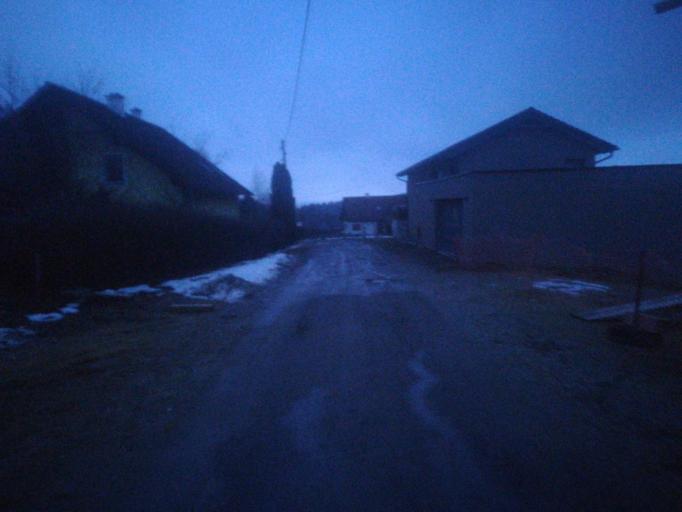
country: AT
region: Upper Austria
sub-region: Politischer Bezirk Perg
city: Perg
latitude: 48.3312
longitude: 14.6145
